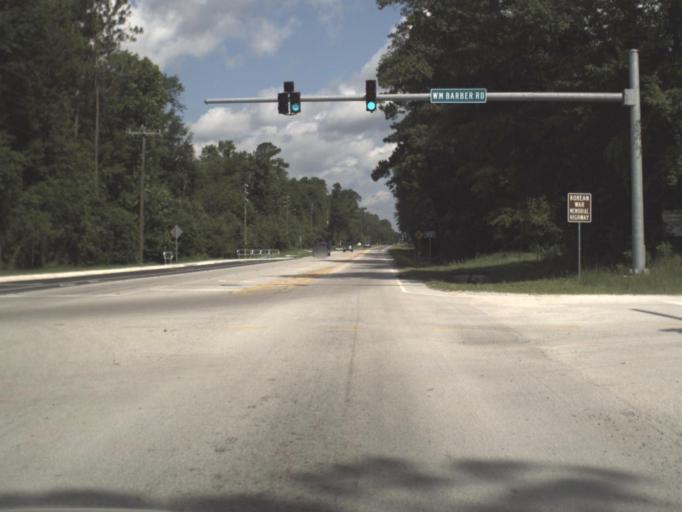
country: US
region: Florida
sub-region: Baker County
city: Macclenny
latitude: 30.2654
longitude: -82.1086
